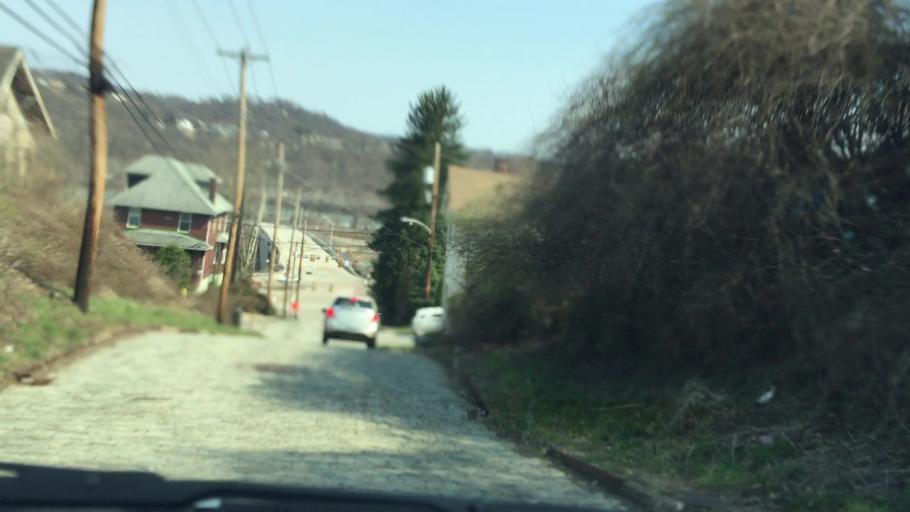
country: US
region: Pennsylvania
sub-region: Allegheny County
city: West Mifflin
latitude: 40.3646
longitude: -79.8448
